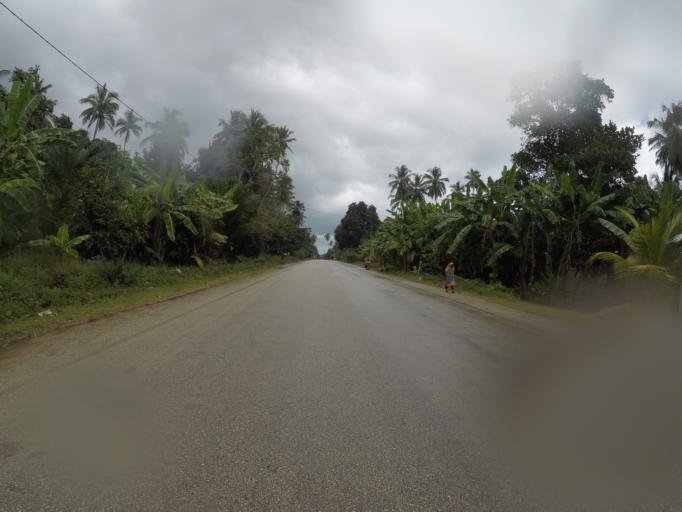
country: TZ
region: Zanzibar North
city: Mkokotoni
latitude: -5.9719
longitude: 39.1965
